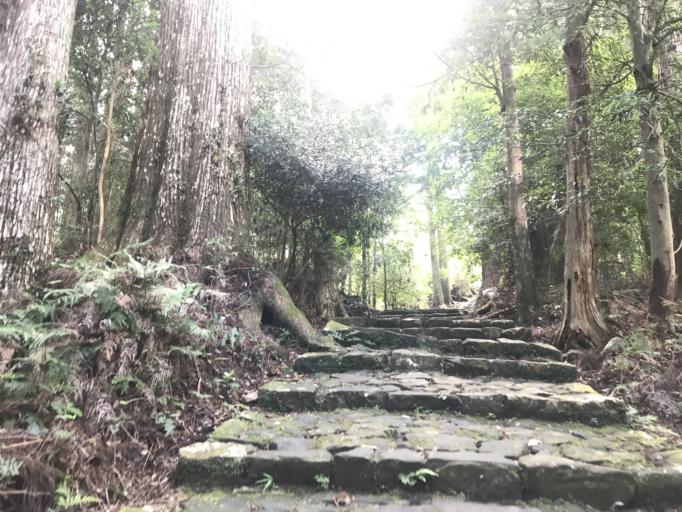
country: JP
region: Wakayama
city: Shingu
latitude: 33.6694
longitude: 135.8942
